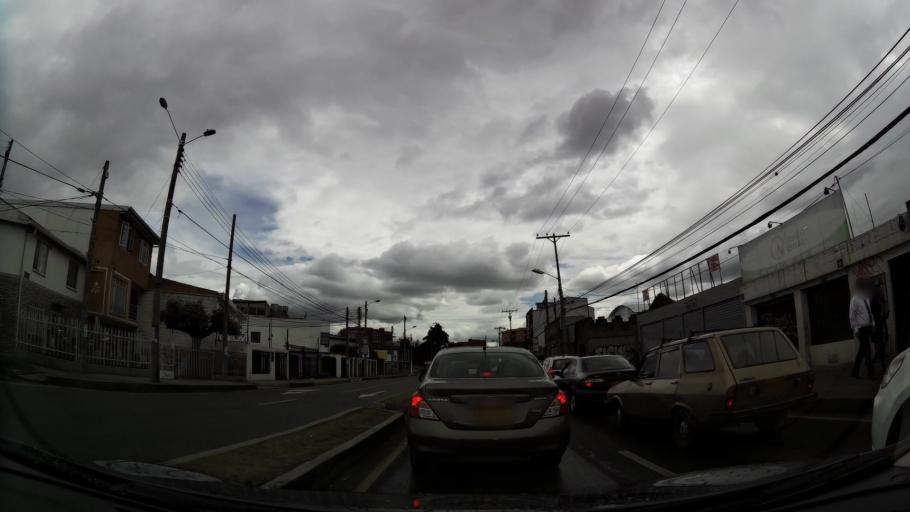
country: CO
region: Bogota D.C.
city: Barrio San Luis
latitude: 4.6984
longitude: -74.0922
